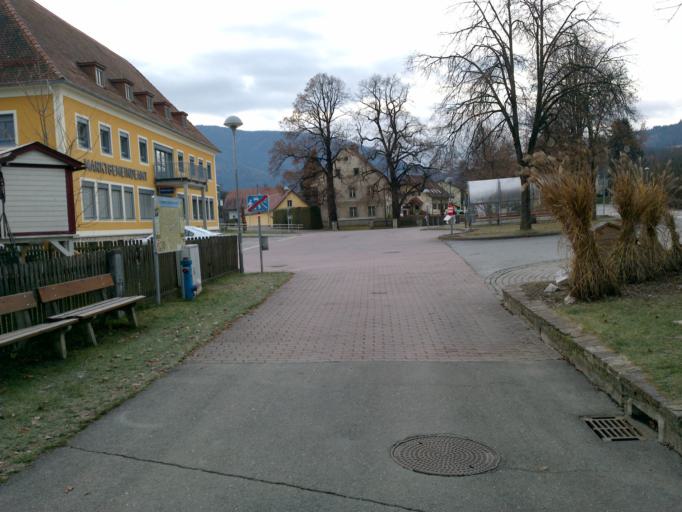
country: AT
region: Styria
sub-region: Politischer Bezirk Murtal
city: Weisskirchen in Steiermark
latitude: 47.1526
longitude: 14.7388
